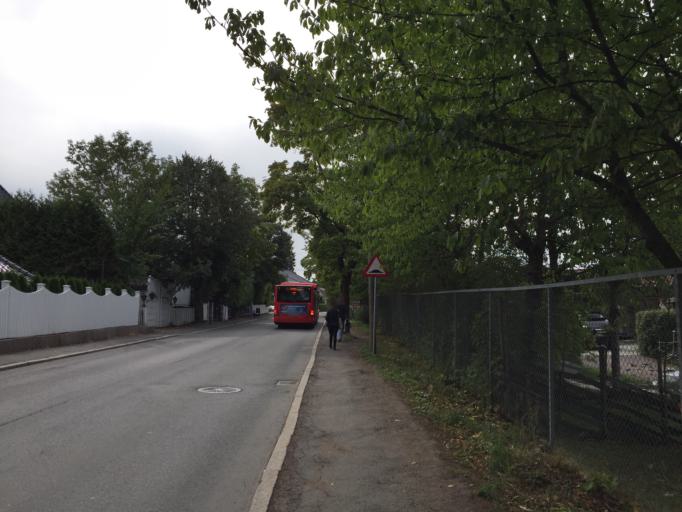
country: NO
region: Oslo
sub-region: Oslo
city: Sjolyststranda
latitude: 59.9055
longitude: 10.6870
